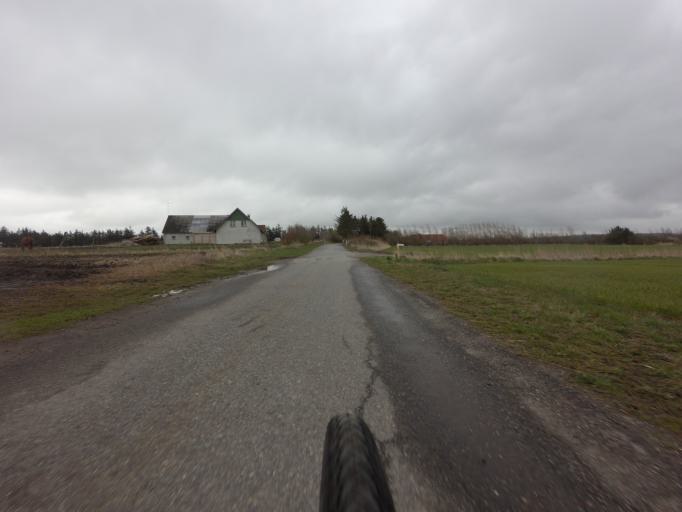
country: DK
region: North Denmark
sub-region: Jammerbugt Kommune
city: Pandrup
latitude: 57.3229
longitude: 9.7909
